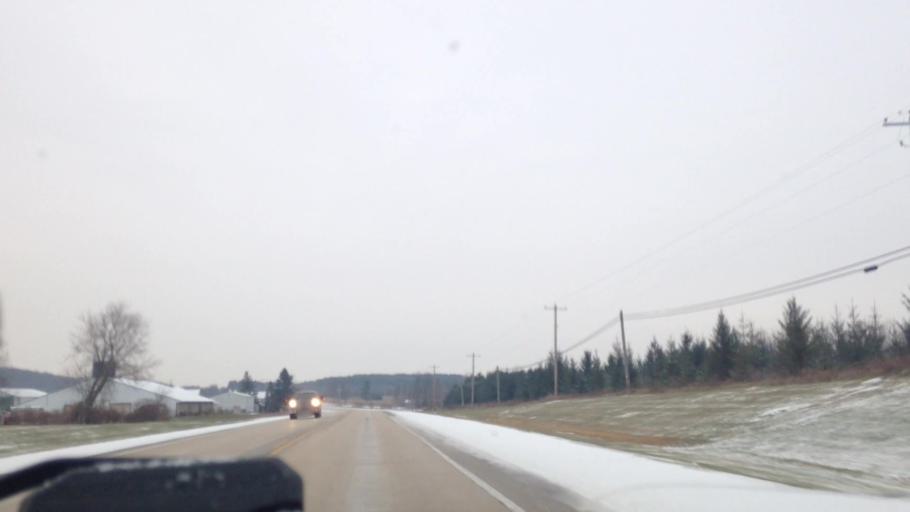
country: US
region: Wisconsin
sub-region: Dodge County
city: Mayville
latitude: 43.4695
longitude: -88.5464
